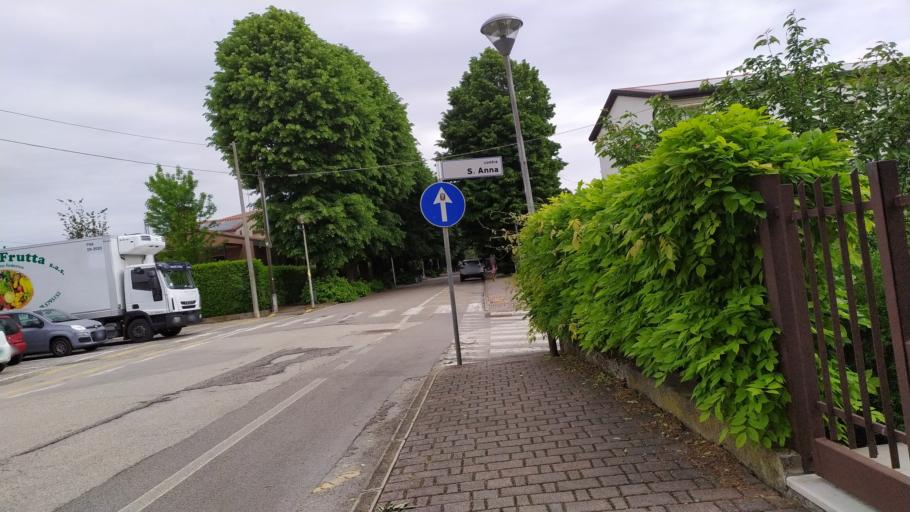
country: IT
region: Veneto
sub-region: Provincia di Padova
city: Camposampiero
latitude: 45.5696
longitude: 11.9292
